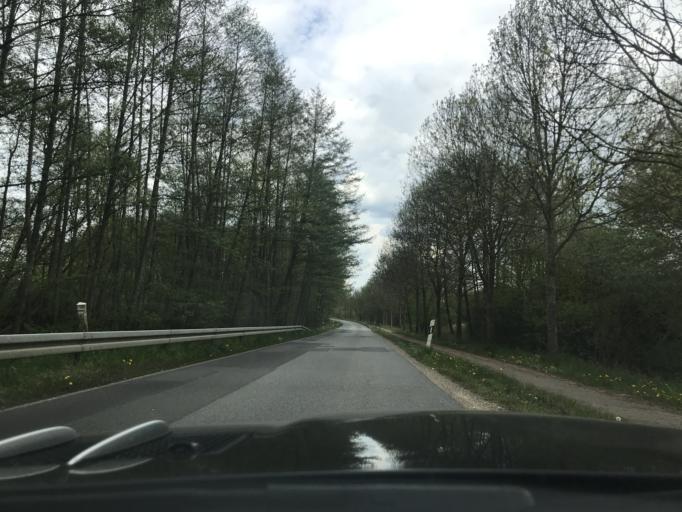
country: DE
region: Schleswig-Holstein
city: Gross Gronau
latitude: 53.7739
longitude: 10.7703
